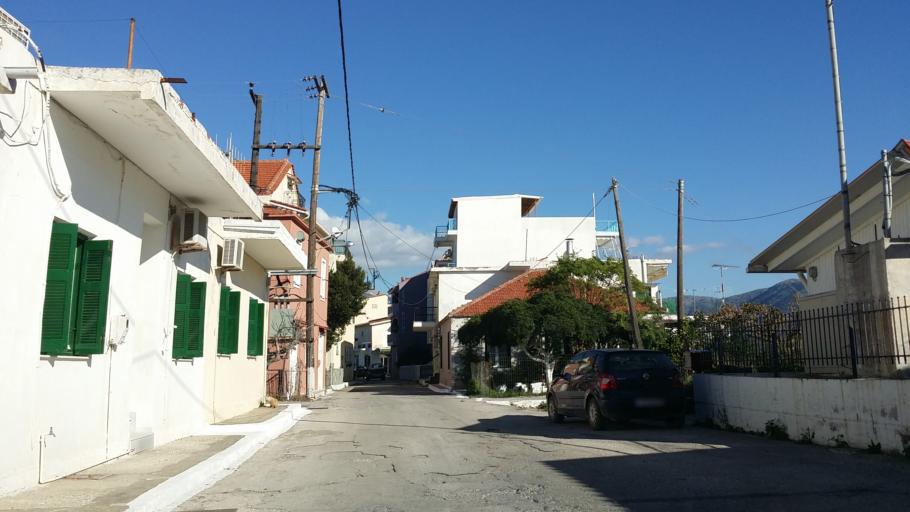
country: GR
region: West Greece
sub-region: Nomos Aitolias kai Akarnanias
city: Kandila
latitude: 38.6672
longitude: 20.9457
